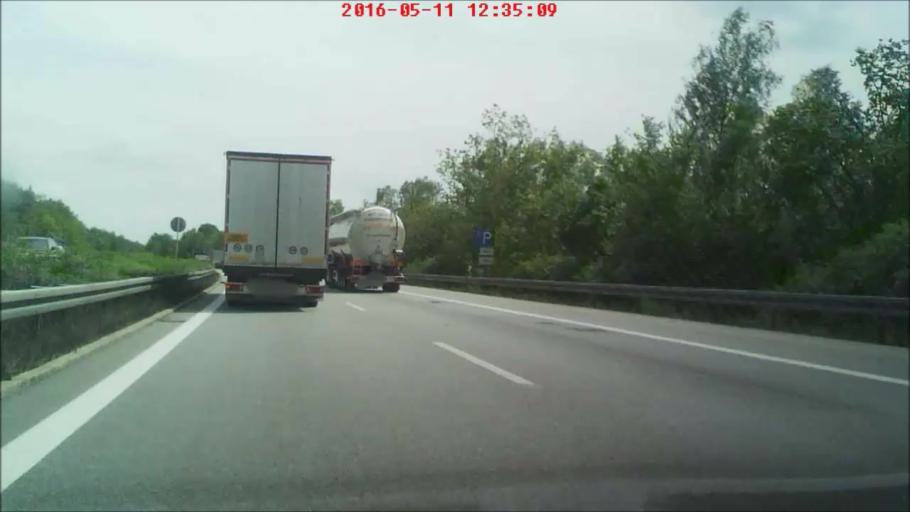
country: DE
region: Bavaria
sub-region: Lower Bavaria
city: Aicha vorm Wald
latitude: 48.6609
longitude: 13.2682
